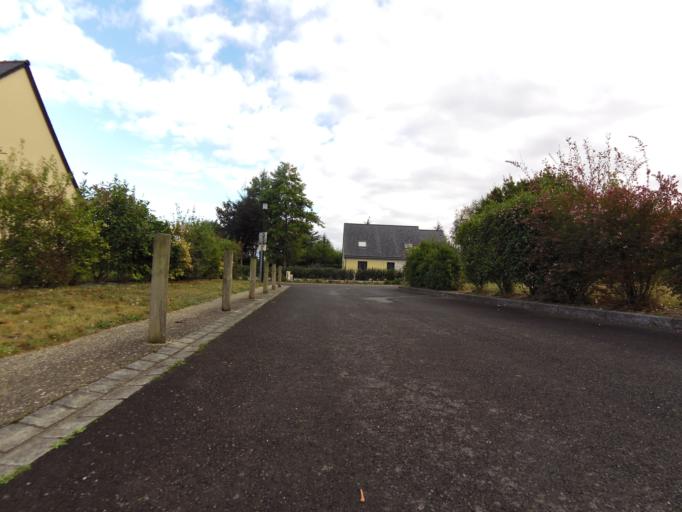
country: FR
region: Brittany
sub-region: Departement d'Ille-et-Vilaine
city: Crevin
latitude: 47.9398
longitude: -1.6570
